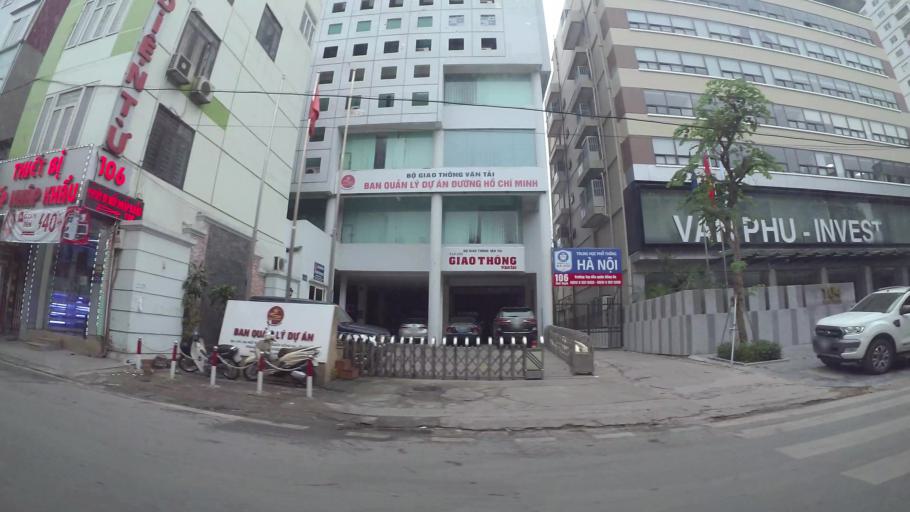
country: VN
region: Ha Noi
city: Dong Da
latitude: 21.0094
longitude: 105.8194
